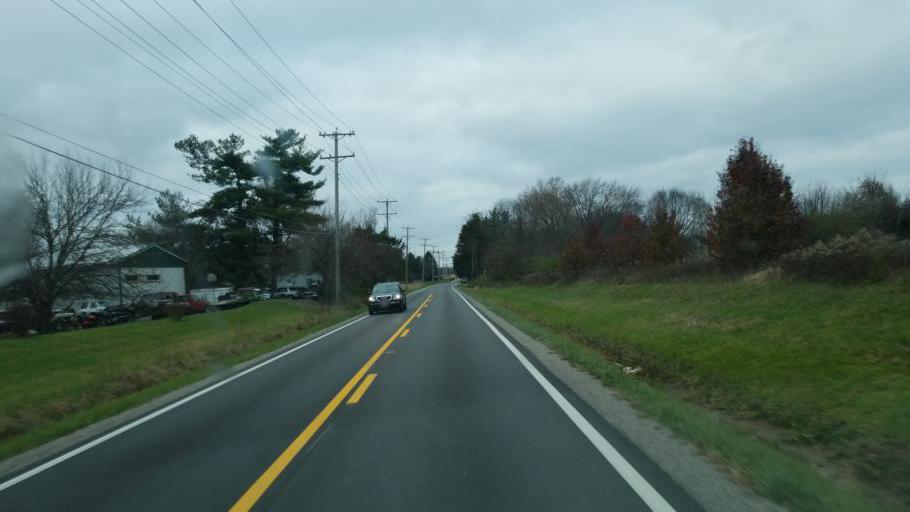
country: US
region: Ohio
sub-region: Franklin County
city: New Albany
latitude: 40.1178
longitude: -82.8391
